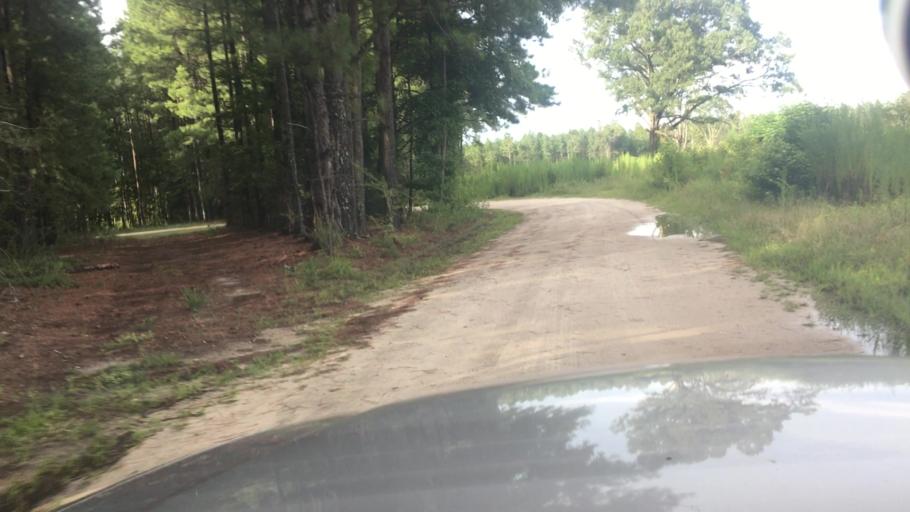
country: US
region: North Carolina
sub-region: Cumberland County
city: Eastover
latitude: 35.1558
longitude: -78.8519
